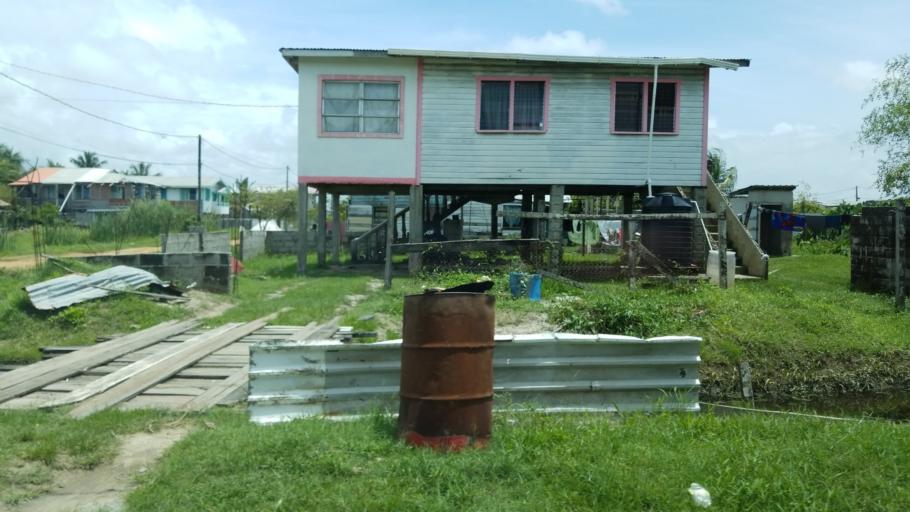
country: GY
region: Demerara-Mahaica
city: Georgetown
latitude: 6.7948
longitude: -58.1197
